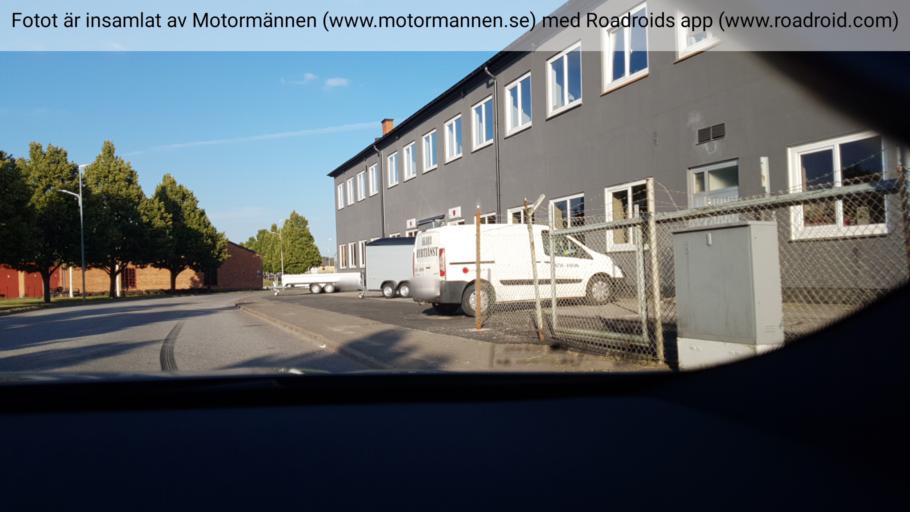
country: SE
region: Vaestra Goetaland
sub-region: Skara Kommun
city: Skara
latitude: 58.3830
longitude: 13.4487
